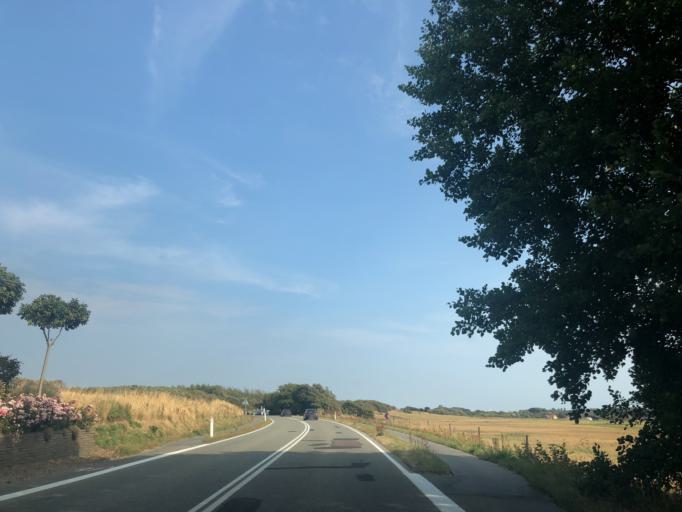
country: DK
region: North Denmark
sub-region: Morso Kommune
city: Nykobing Mors
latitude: 56.7955
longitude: 9.0361
